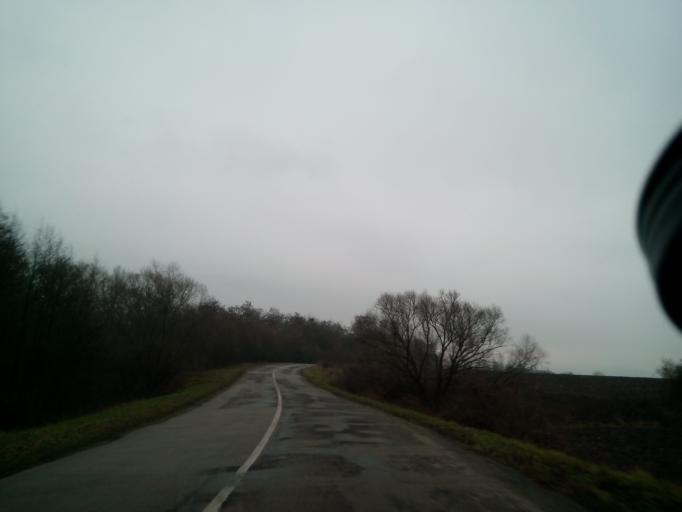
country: SK
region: Kosicky
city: Kosice
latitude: 48.7204
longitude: 21.4373
